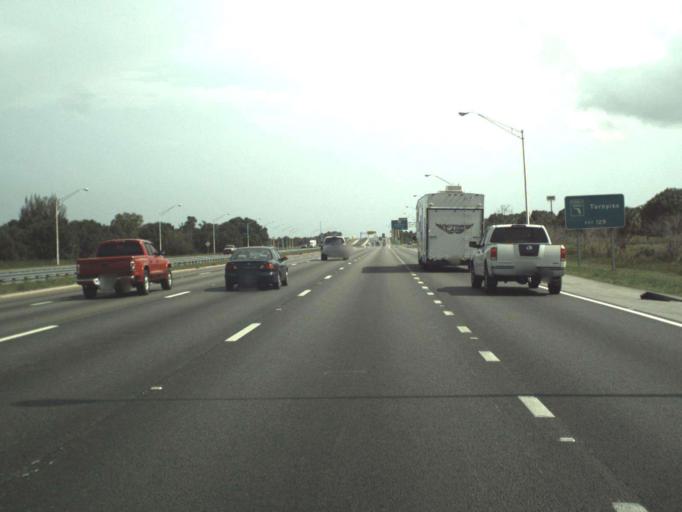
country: US
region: Florida
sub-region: Saint Lucie County
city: Fort Pierce South
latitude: 27.4257
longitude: -80.3886
